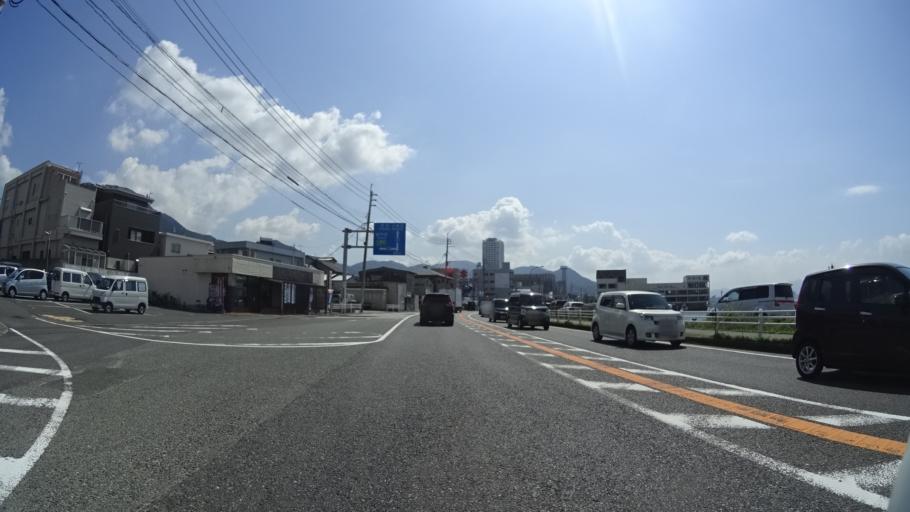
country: JP
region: Yamaguchi
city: Shimonoseki
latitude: 33.9102
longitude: 130.9339
